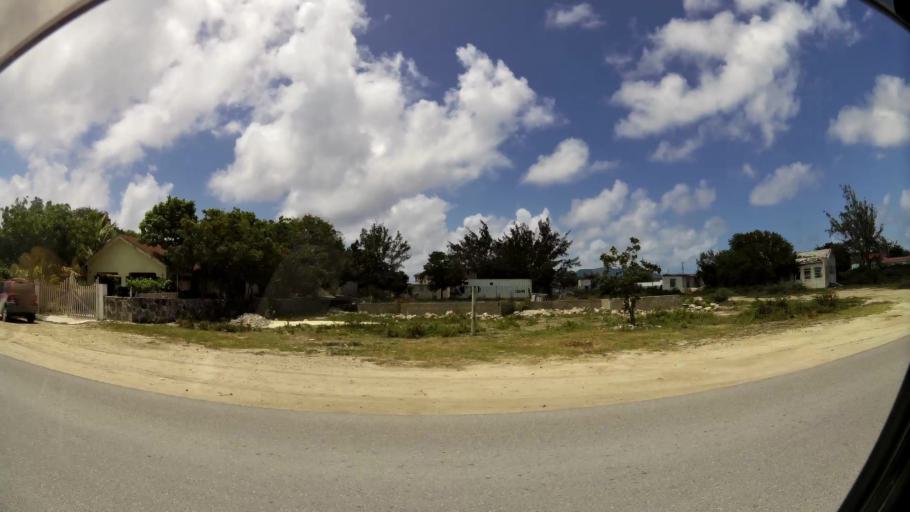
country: TC
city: Cockburn Town
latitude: 21.4519
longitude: -71.1451
